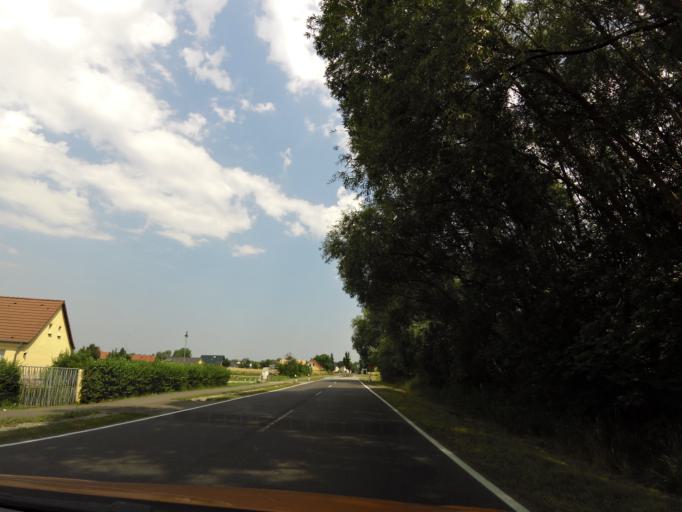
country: DE
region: Brandenburg
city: Wustermark
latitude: 52.5115
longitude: 12.9324
